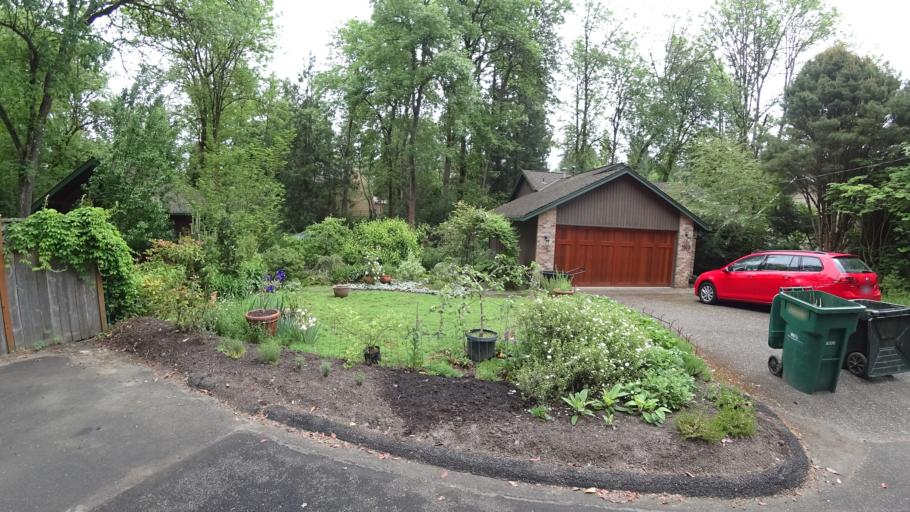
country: US
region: Oregon
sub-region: Washington County
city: Garden Home-Whitford
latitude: 45.4693
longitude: -122.7565
